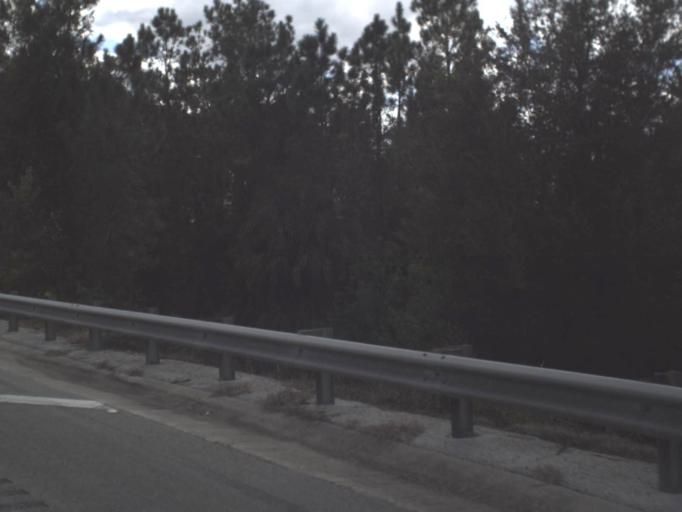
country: US
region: Florida
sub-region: Osceola County
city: Saint Cloud
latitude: 28.1515
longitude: -81.2974
